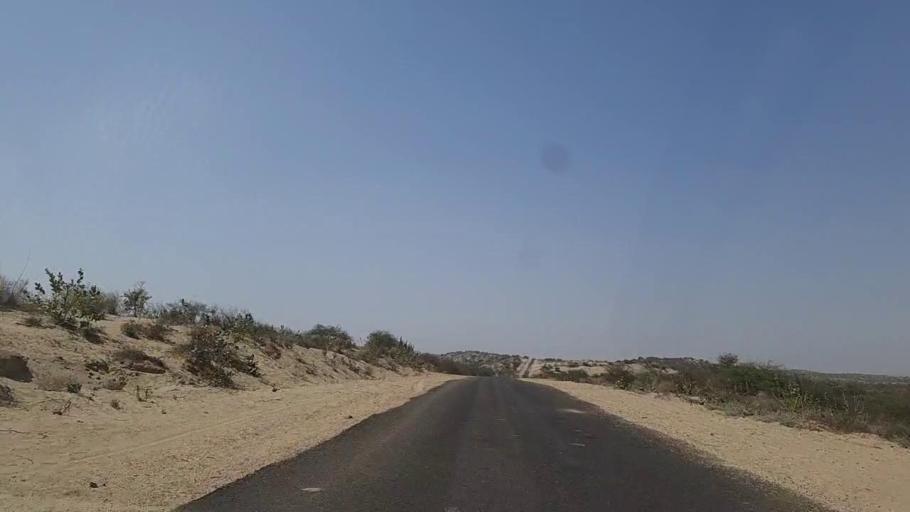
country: PK
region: Sindh
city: Diplo
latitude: 24.5624
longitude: 69.4609
